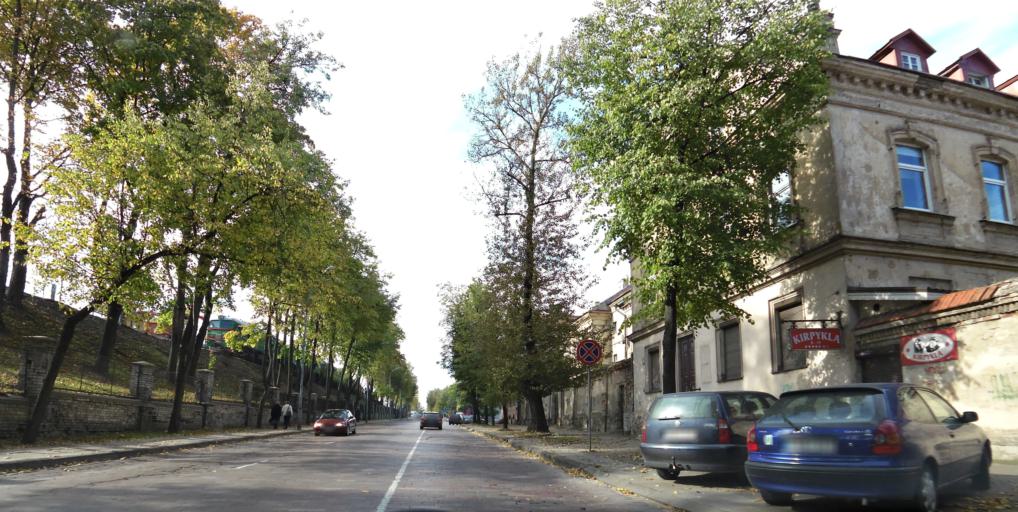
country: LT
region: Vilnius County
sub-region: Vilnius
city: Vilnius
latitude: 54.6720
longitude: 25.2895
